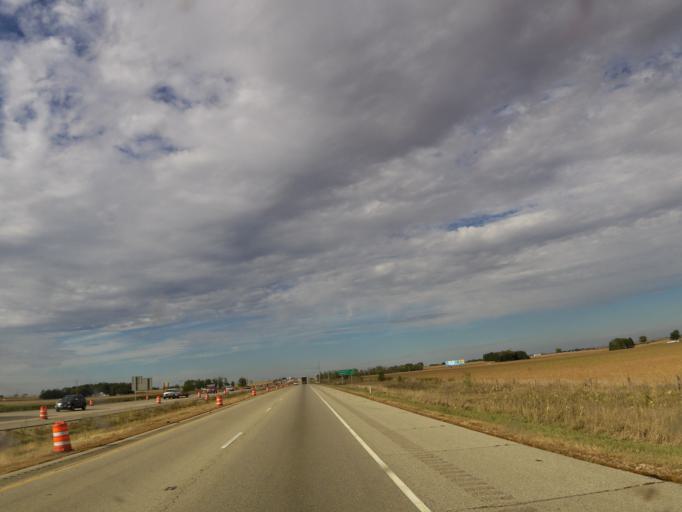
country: US
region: Wisconsin
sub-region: Rock County
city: Beloit
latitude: 42.5764
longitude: -88.9813
